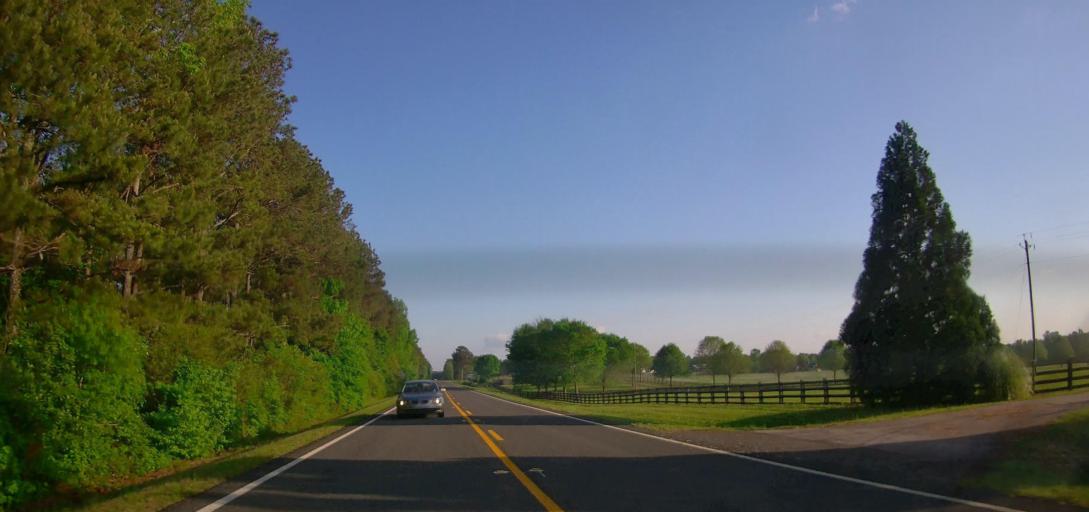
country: US
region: Georgia
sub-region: Walton County
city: Social Circle
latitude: 33.5007
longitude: -83.6518
